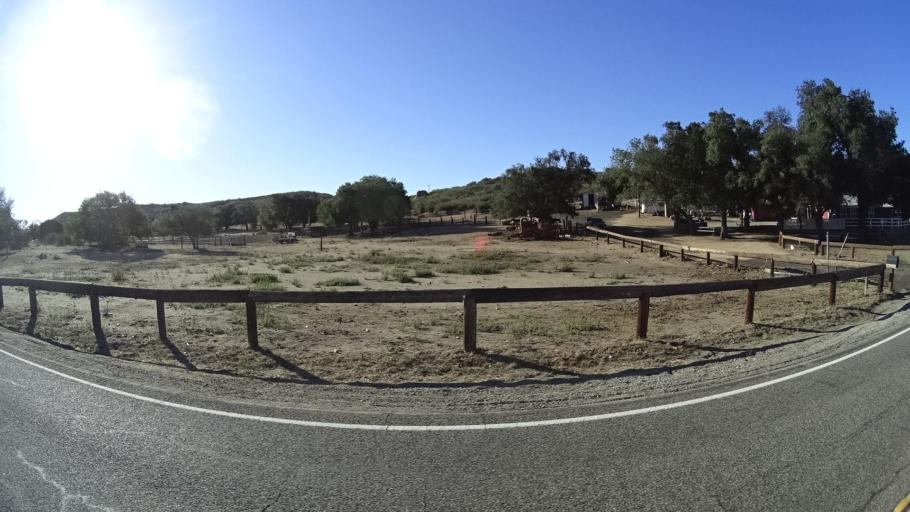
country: MX
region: Baja California
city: Tecate
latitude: 32.5998
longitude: -116.5849
